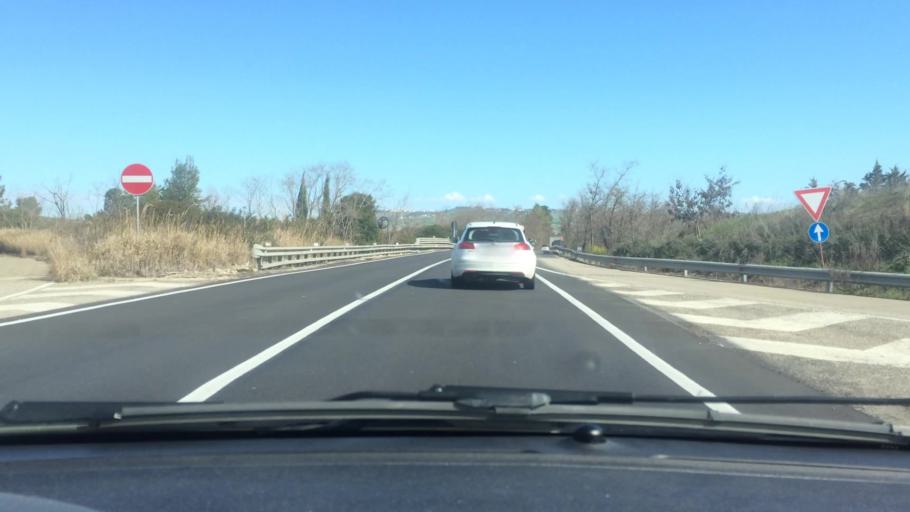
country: IT
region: Basilicate
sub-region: Provincia di Matera
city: La Martella
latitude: 40.6027
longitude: 16.5669
